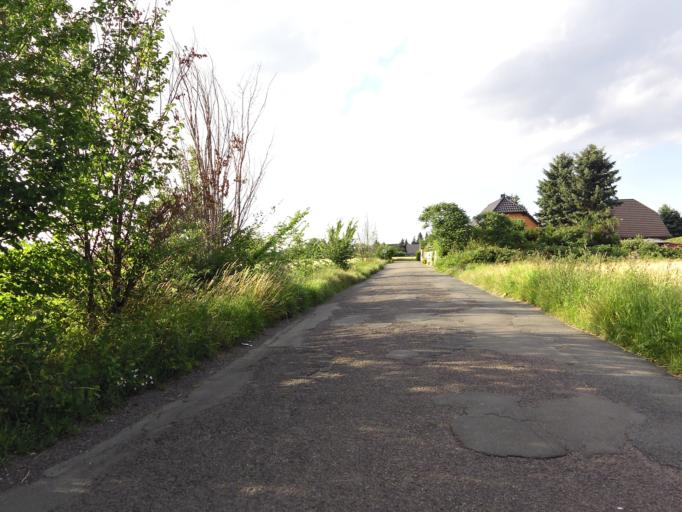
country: DE
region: Saxony
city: Markkleeberg
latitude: 51.2840
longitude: 12.2998
